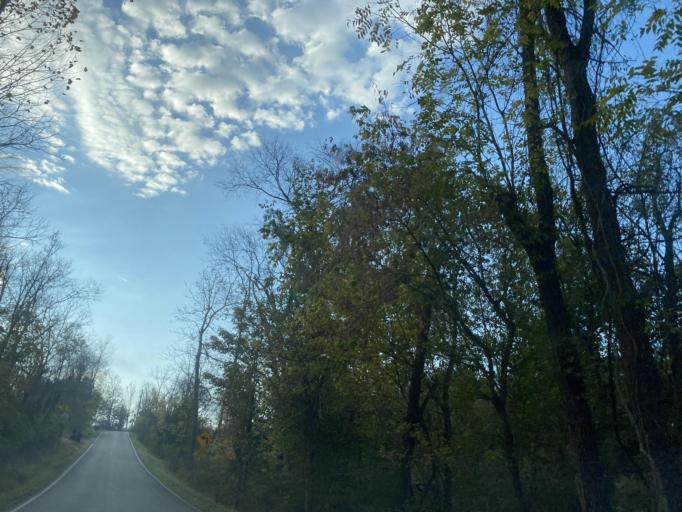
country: US
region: Kentucky
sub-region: Pendleton County
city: Falmouth
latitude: 38.7503
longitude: -84.3383
